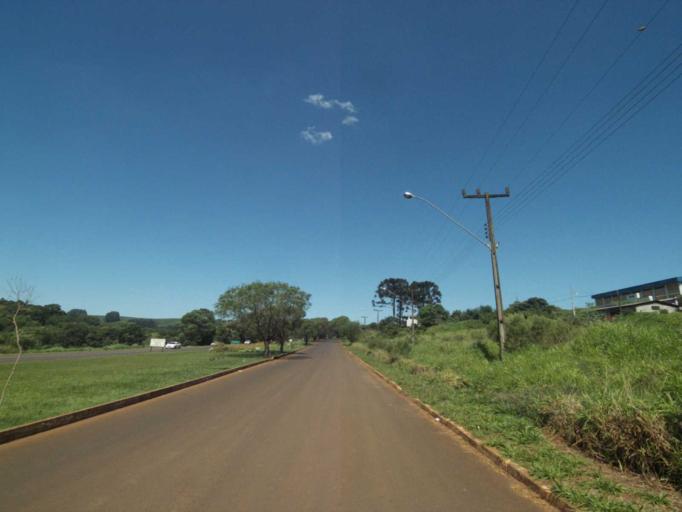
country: BR
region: Parana
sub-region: Laranjeiras Do Sul
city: Laranjeiras do Sul
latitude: -25.3794
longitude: -52.2082
